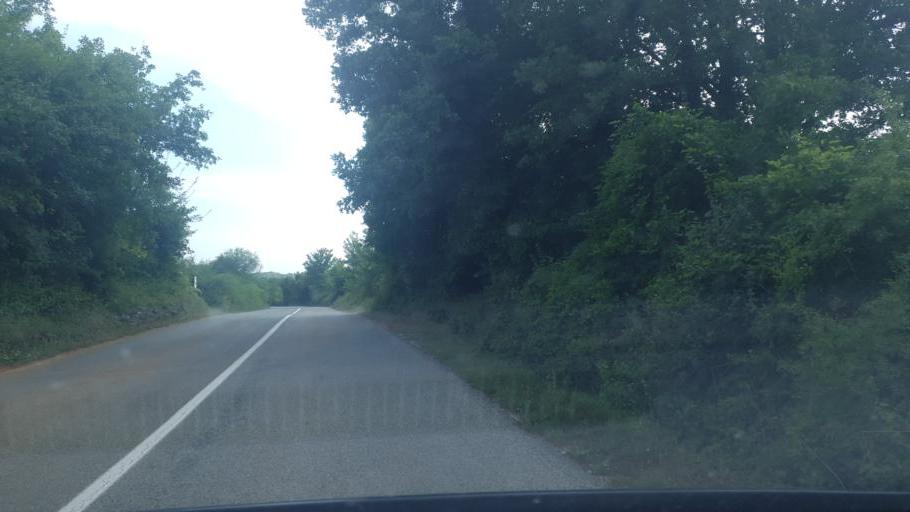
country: HR
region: Primorsko-Goranska
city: Punat
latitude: 45.0981
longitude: 14.6408
